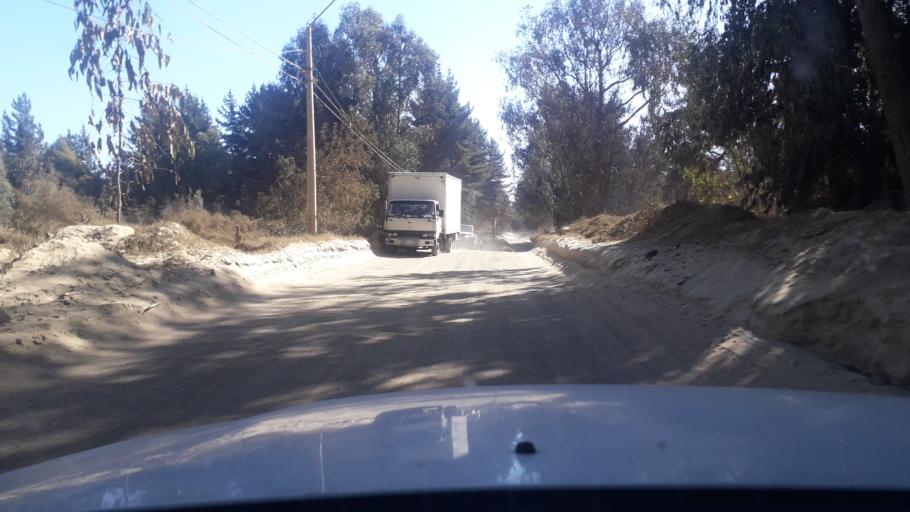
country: CL
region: Valparaiso
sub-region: Provincia de Valparaiso
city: Vina del Mar
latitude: -32.9573
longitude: -71.5178
